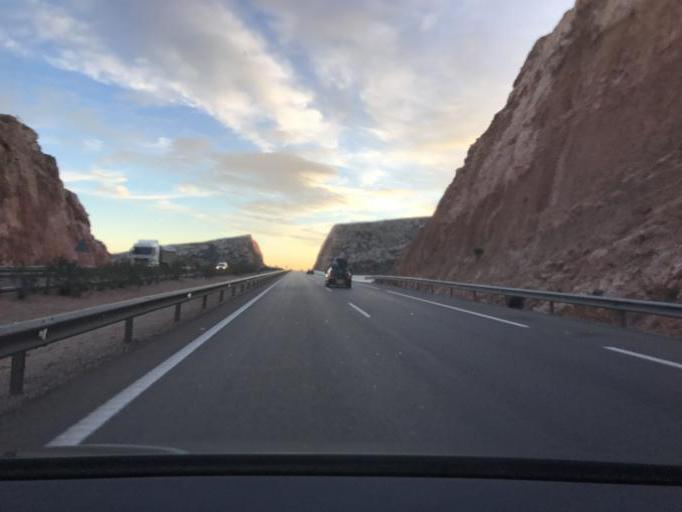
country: ES
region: Andalusia
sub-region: Provincia de Almeria
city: Almeria
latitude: 36.8434
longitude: -2.4846
